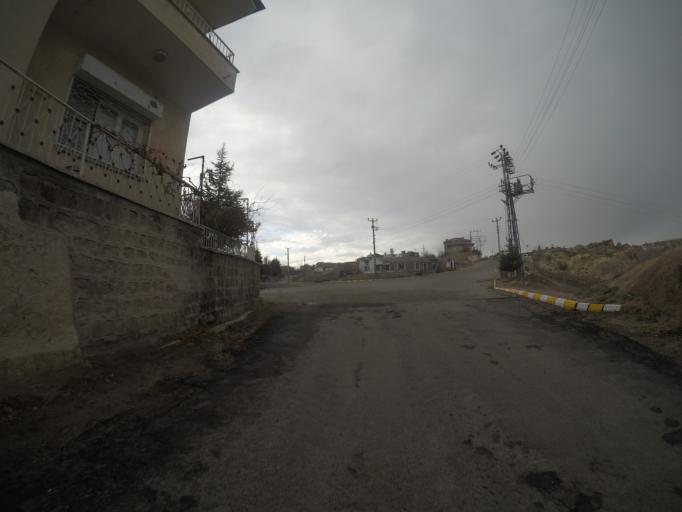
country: TR
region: Nevsehir
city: Goereme
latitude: 38.6262
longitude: 34.8601
